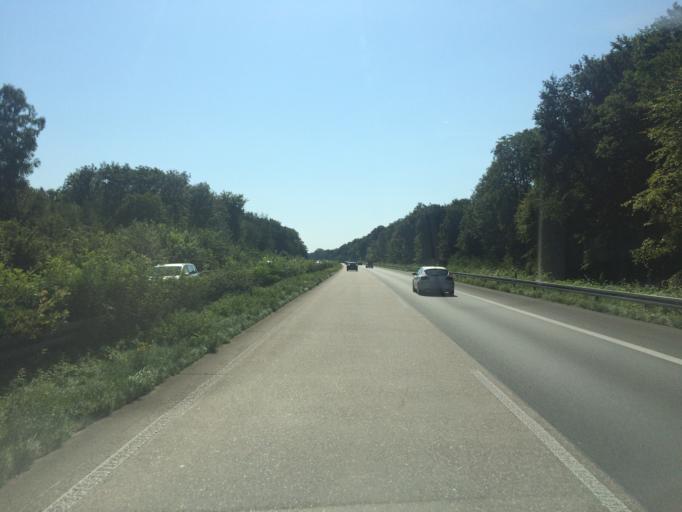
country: DE
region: North Rhine-Westphalia
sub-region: Regierungsbezirk Munster
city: Senden
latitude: 51.8552
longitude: 7.5779
